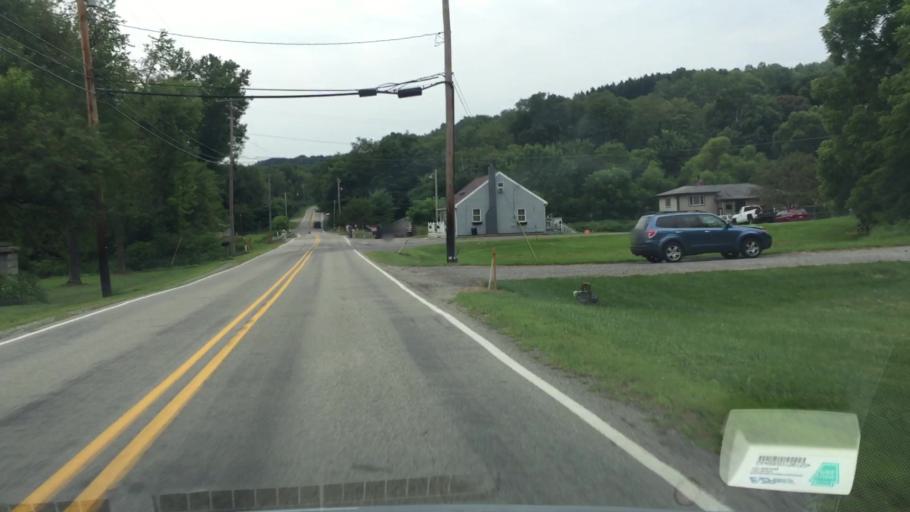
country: US
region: Pennsylvania
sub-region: Allegheny County
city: Curtisville
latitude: 40.6754
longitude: -79.8290
